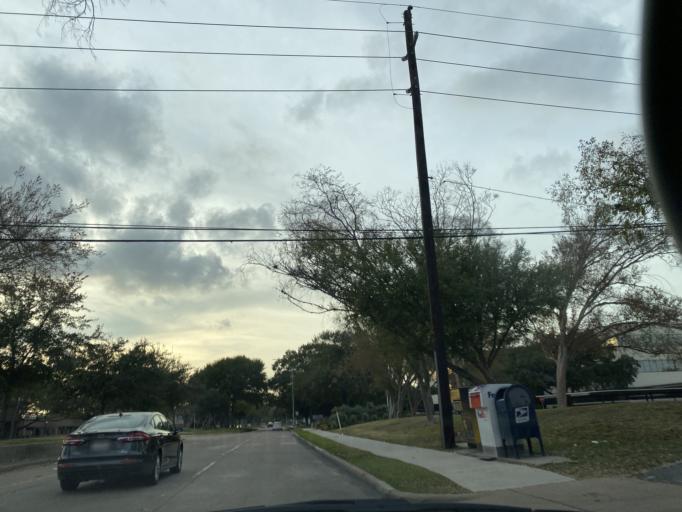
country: US
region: Texas
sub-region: Harris County
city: Bunker Hill Village
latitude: 29.7278
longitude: -95.5611
